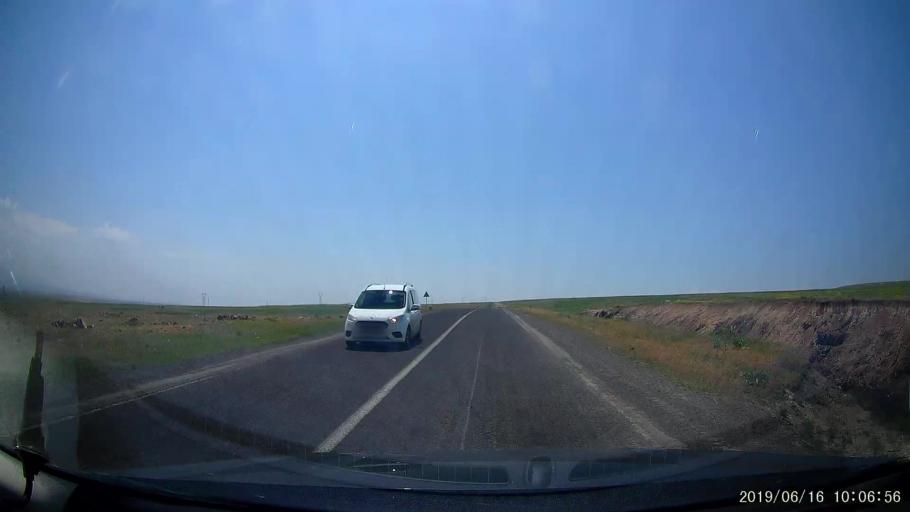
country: TR
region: Kars
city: Digor
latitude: 40.2495
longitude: 43.5490
